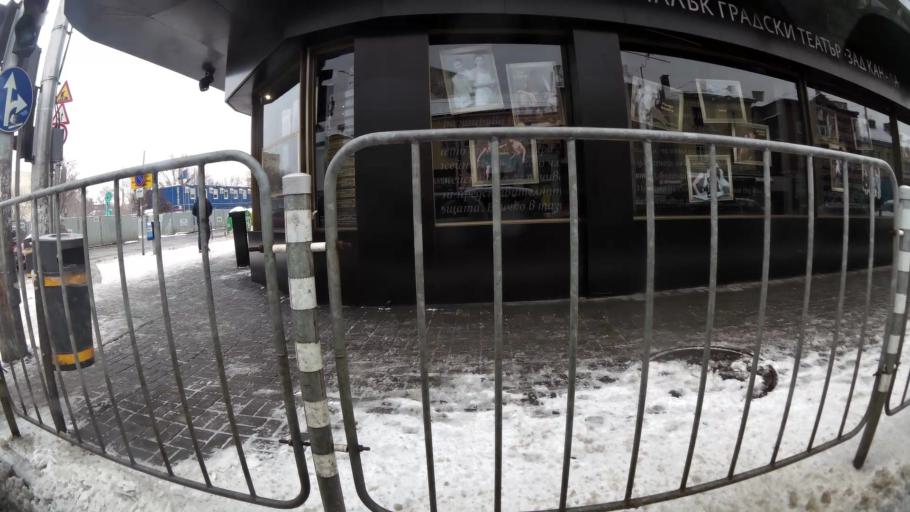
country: BG
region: Sofia-Capital
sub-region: Stolichna Obshtina
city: Sofia
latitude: 42.6963
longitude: 23.3473
